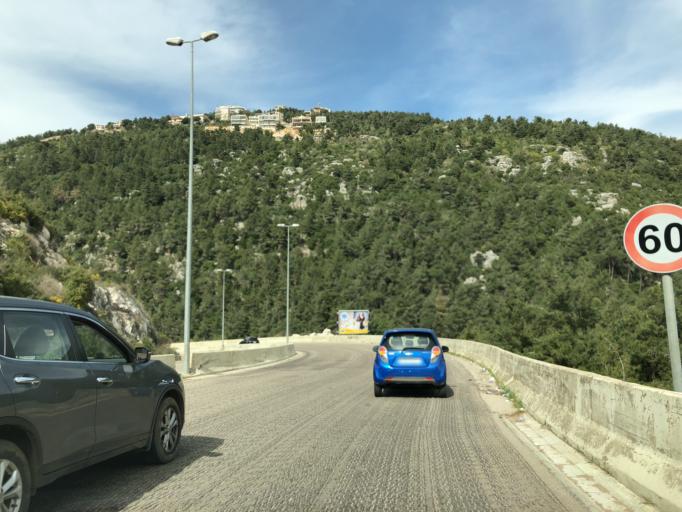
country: LB
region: Mont-Liban
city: Bhamdoun el Mhatta
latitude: 33.8933
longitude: 35.6573
